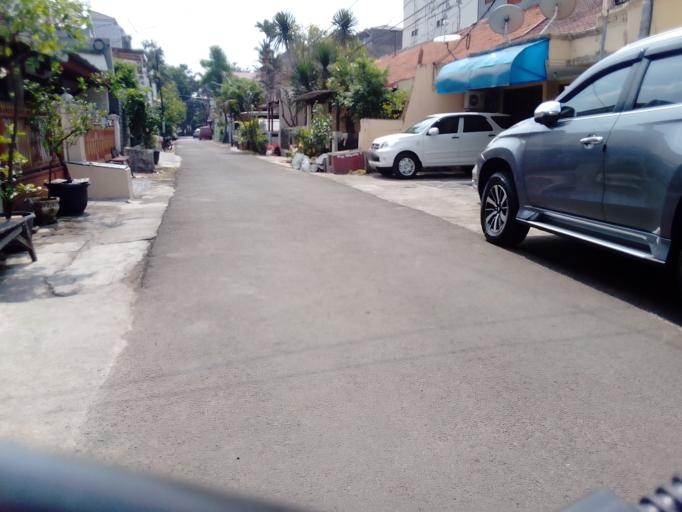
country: ID
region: Jakarta Raya
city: Jakarta
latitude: -6.2089
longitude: 106.8114
